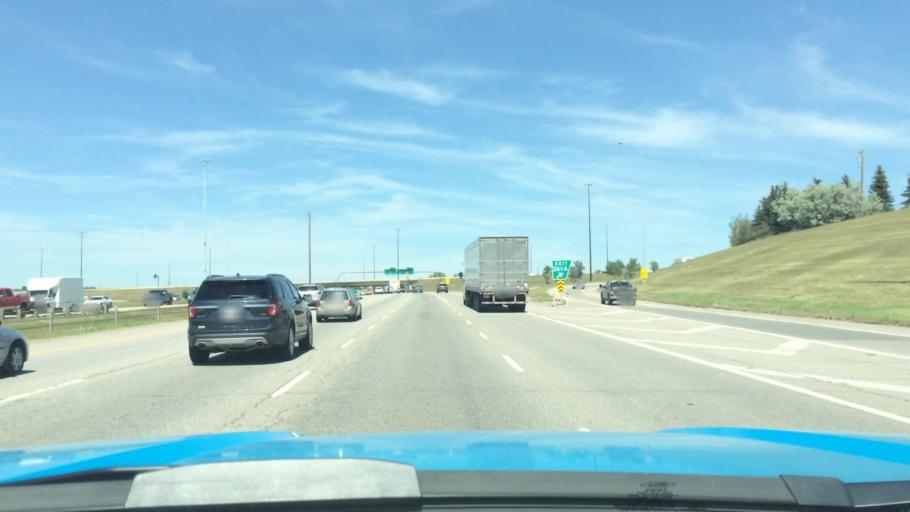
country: CA
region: Alberta
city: Calgary
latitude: 51.0921
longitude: -114.0393
